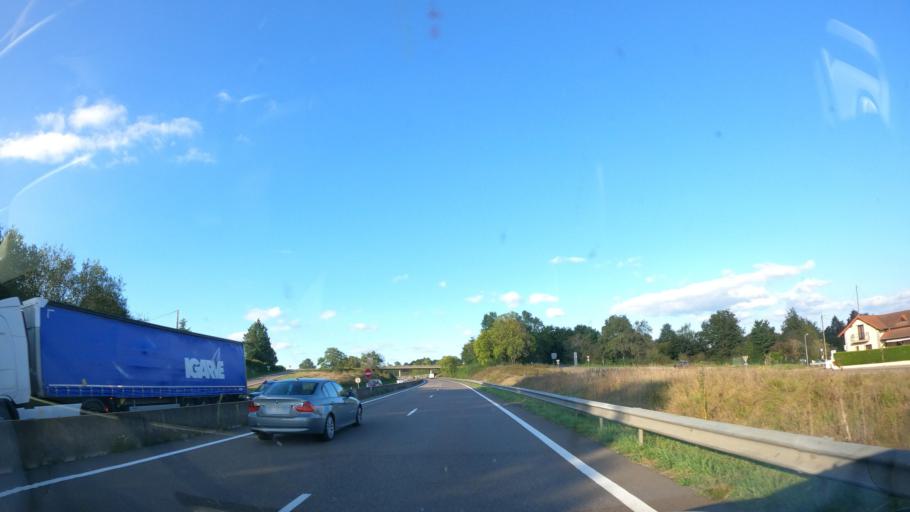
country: FR
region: Bourgogne
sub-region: Departement de Saone-et-Loire
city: Saint-Vallier
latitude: 46.6419
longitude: 4.3290
